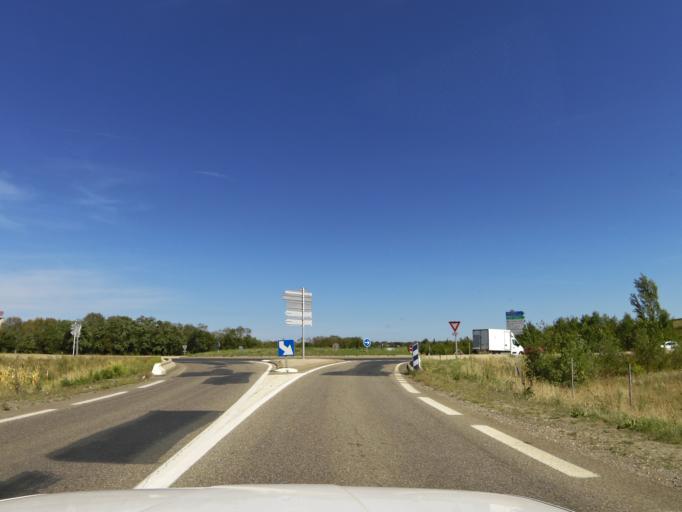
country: FR
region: Rhone-Alpes
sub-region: Departement du Rhone
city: Saint-Laurent-de-Mure
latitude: 45.6939
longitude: 5.0769
